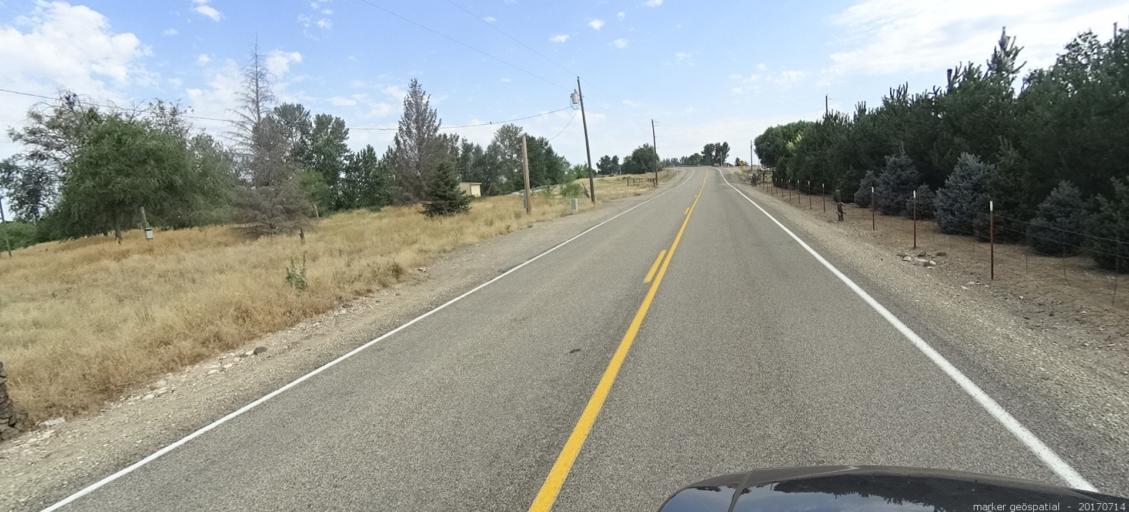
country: US
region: Idaho
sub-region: Ada County
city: Kuna
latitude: 43.4837
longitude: -116.3544
